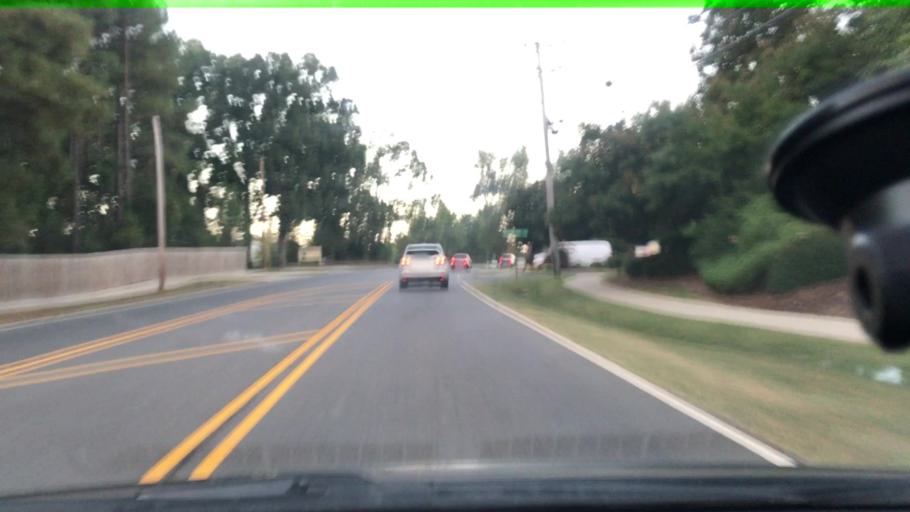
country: US
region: North Carolina
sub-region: Mecklenburg County
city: Cornelius
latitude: 35.4528
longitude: -80.8885
